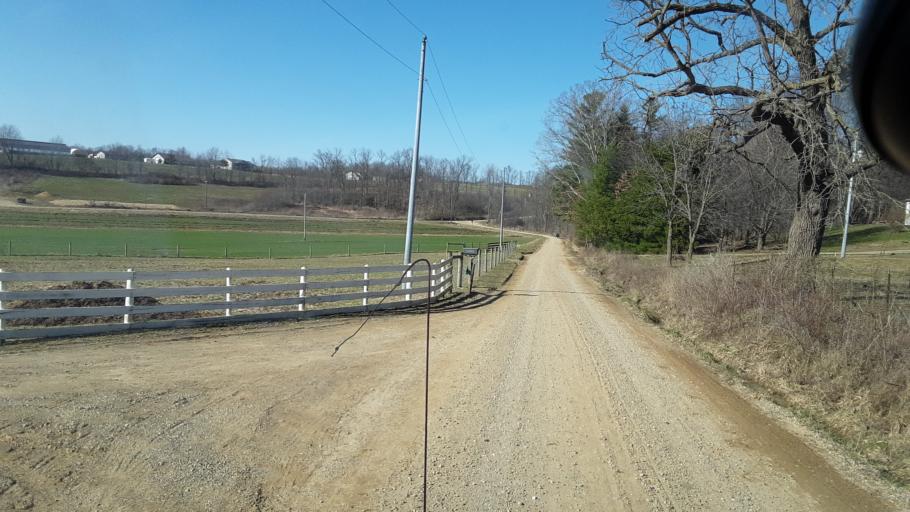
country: US
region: Ohio
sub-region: Knox County
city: Oak Hill
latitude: 40.3263
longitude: -82.1913
